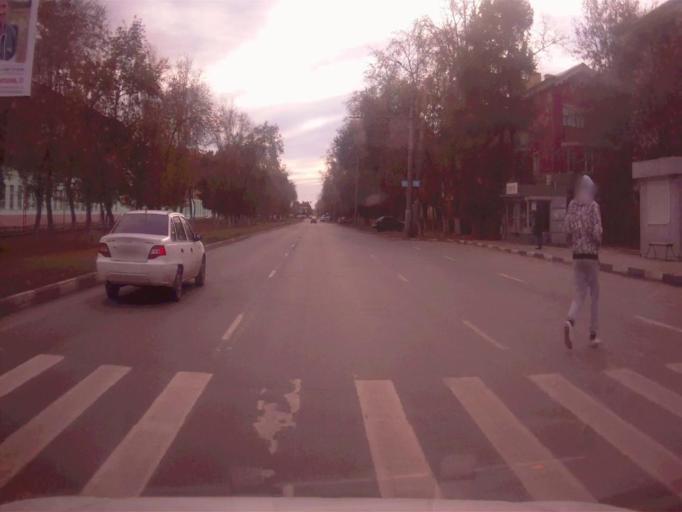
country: RU
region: Chelyabinsk
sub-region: Gorod Chelyabinsk
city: Chelyabinsk
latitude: 55.1208
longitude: 61.4725
